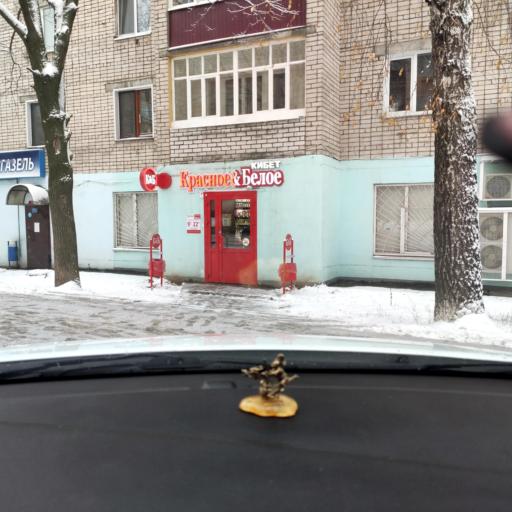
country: RU
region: Tatarstan
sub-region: Zelenodol'skiy Rayon
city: Zelenodolsk
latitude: 55.8508
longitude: 48.5252
